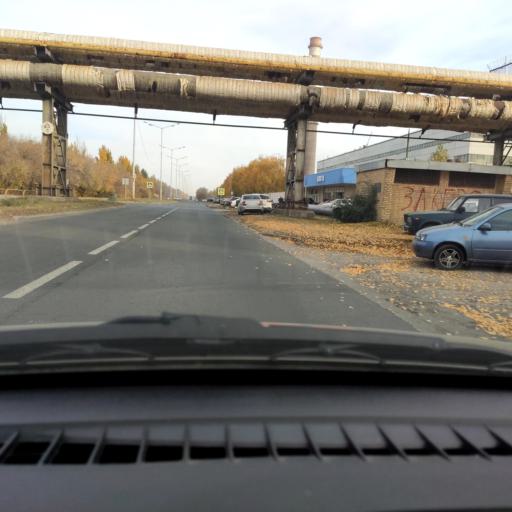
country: RU
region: Samara
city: Tol'yatti
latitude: 53.5703
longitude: 49.2485
